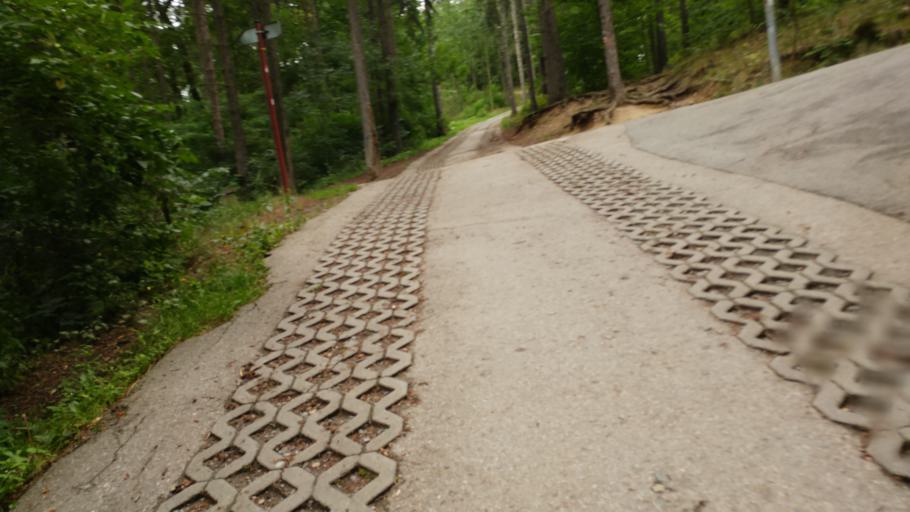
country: CZ
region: Central Bohemia
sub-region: Okres Praha-Zapad
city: Pruhonice
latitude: 50.0436
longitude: 14.5295
